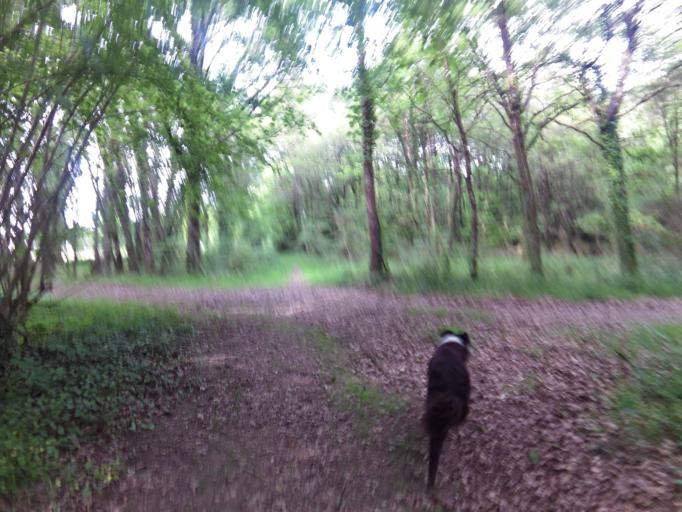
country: FR
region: Brittany
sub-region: Departement du Morbihan
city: Molac
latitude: 47.7620
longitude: -2.4319
